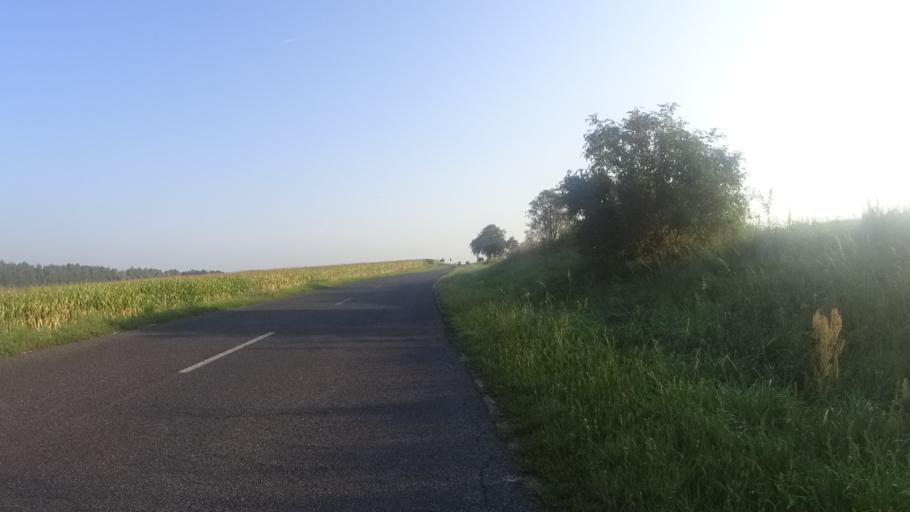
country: HU
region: Zala
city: Zalakomar
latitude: 46.5771
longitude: 17.1770
